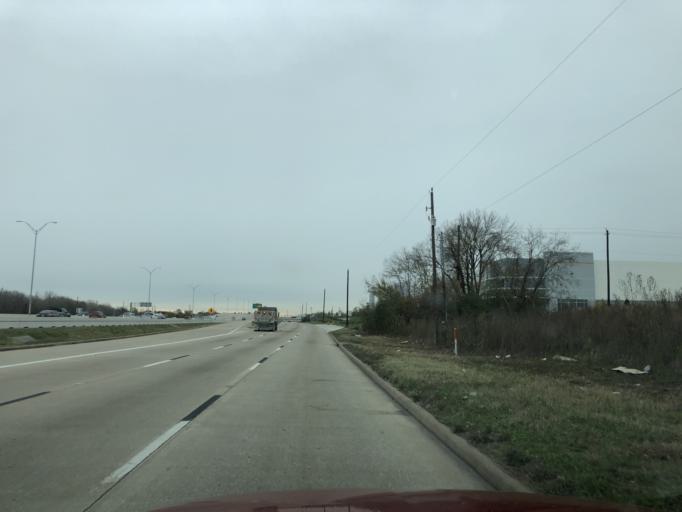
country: US
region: Texas
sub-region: Fort Bend County
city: Missouri City
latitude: 29.6313
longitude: -95.5245
